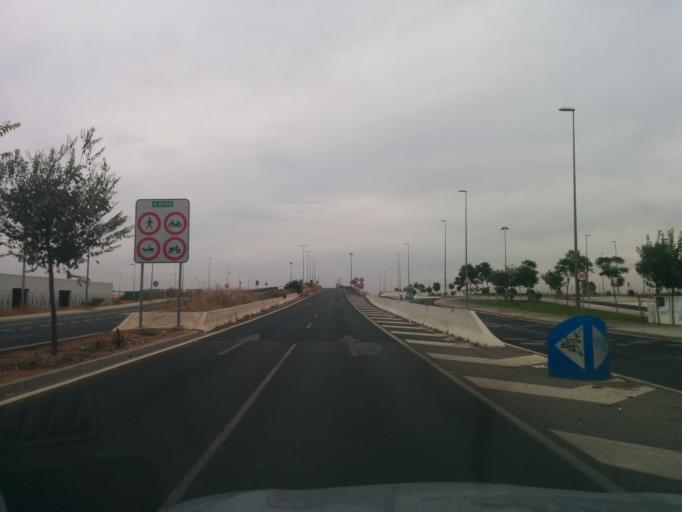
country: ES
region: Andalusia
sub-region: Provincia de Sevilla
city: La Algaba
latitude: 37.4328
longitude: -5.9752
